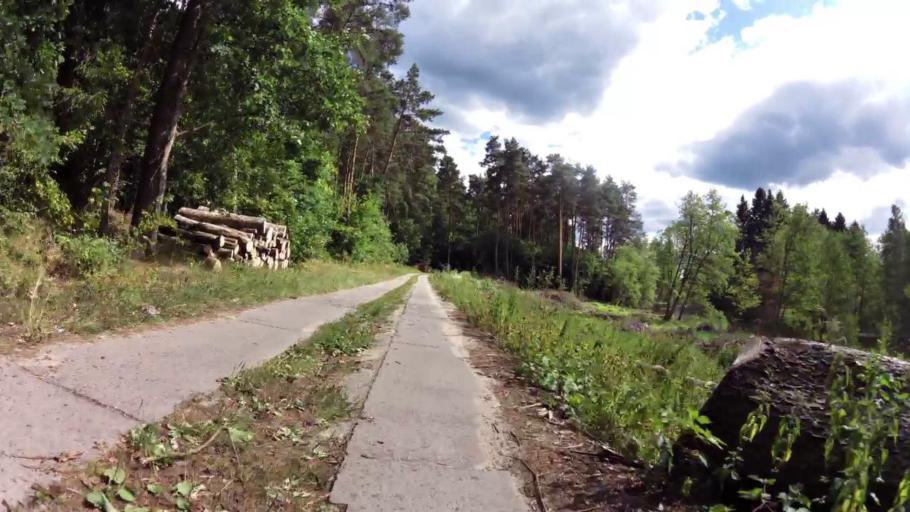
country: PL
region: West Pomeranian Voivodeship
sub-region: Powiat lobeski
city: Lobez
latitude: 53.6474
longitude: 15.5810
